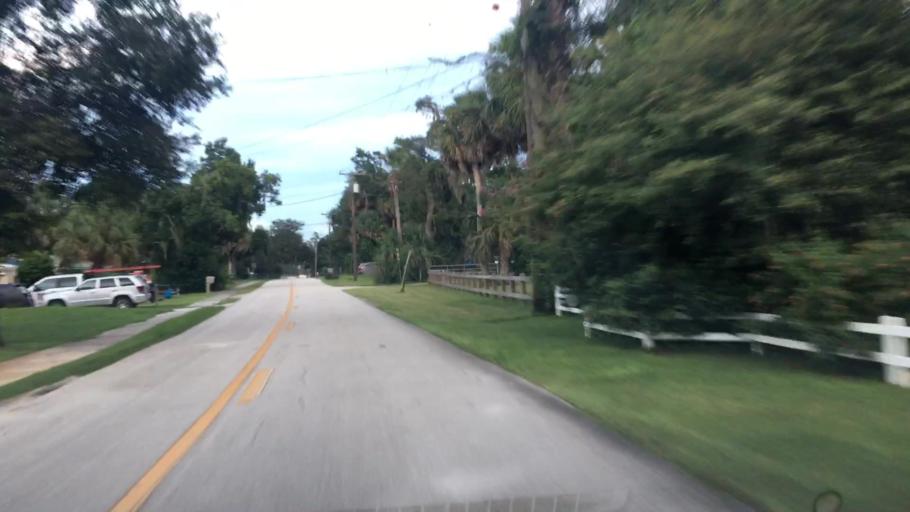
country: US
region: Florida
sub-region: Volusia County
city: DeBary
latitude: 28.8761
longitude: -81.2973
